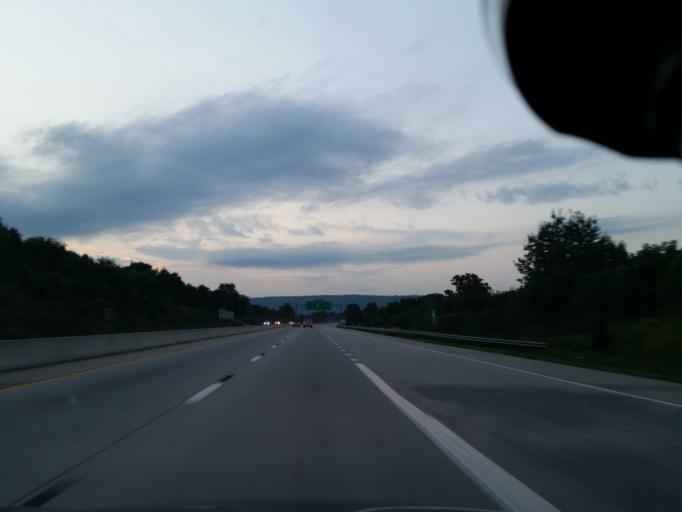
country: US
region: Pennsylvania
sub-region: Cumberland County
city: Mechanicsburg
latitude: 40.2615
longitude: -76.9953
